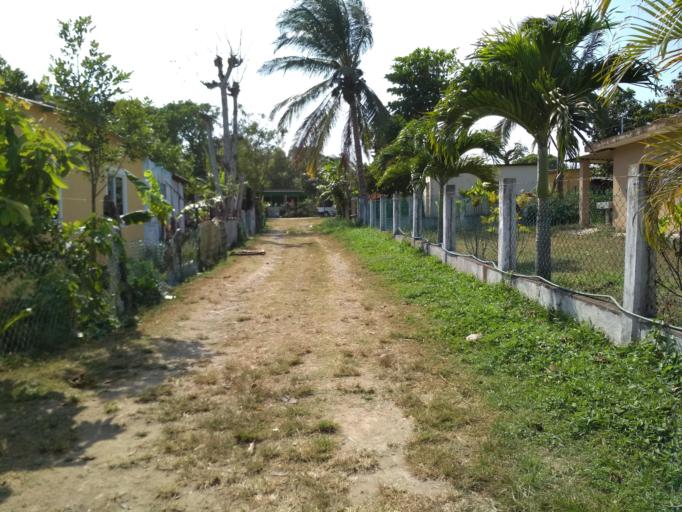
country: MX
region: Veracruz
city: Manlio Fabio Altamirano
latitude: 19.1514
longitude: -96.3068
